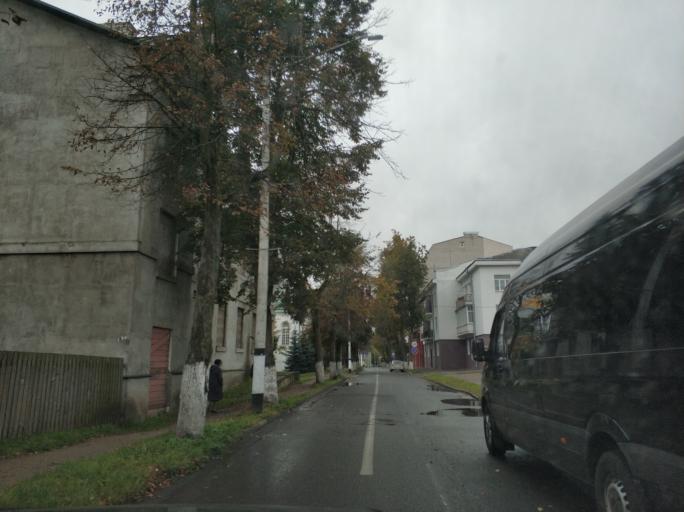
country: BY
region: Vitebsk
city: Polatsk
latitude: 55.4840
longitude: 28.7709
